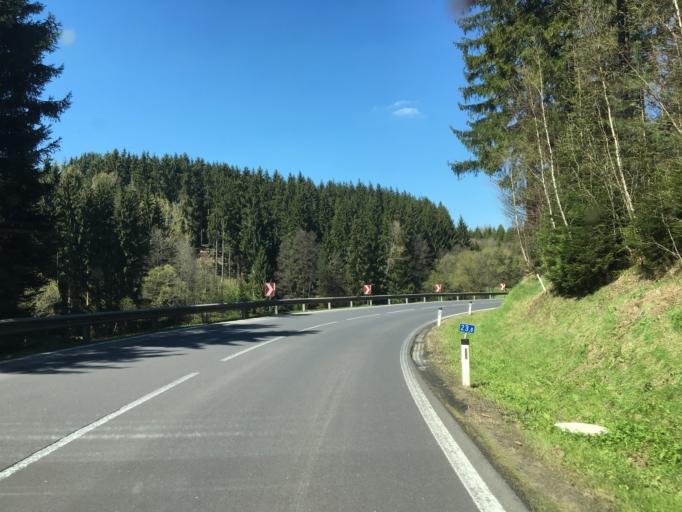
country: AT
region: Upper Austria
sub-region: Politischer Bezirk Urfahr-Umgebung
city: Bad Leonfelden
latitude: 48.4921
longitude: 14.2963
